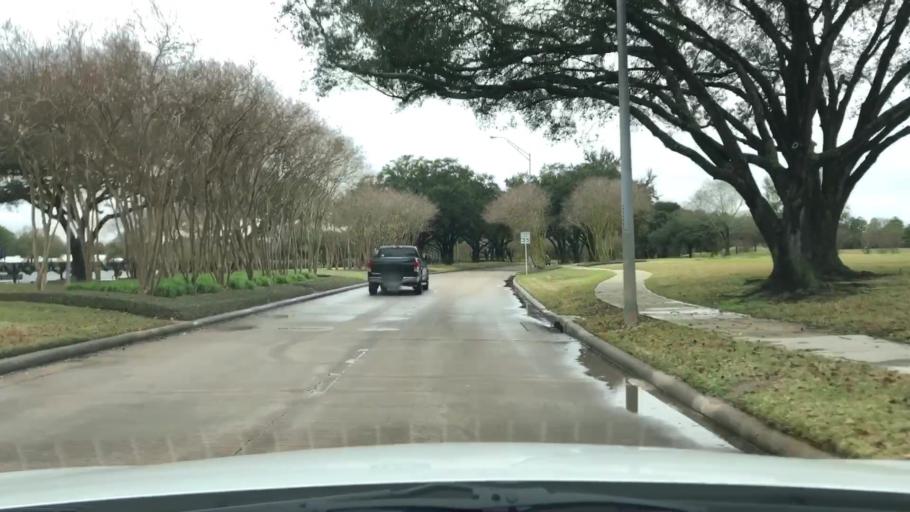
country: US
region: Texas
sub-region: Fort Bend County
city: Cinco Ranch
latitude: 29.7415
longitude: -95.7581
